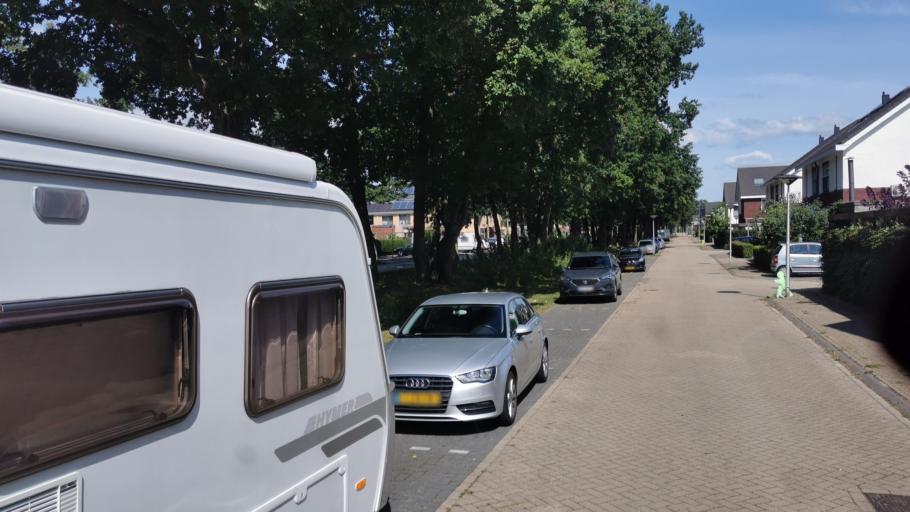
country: DE
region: North Rhine-Westphalia
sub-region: Regierungsbezirk Munster
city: Gronau
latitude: 52.2090
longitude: 6.9596
